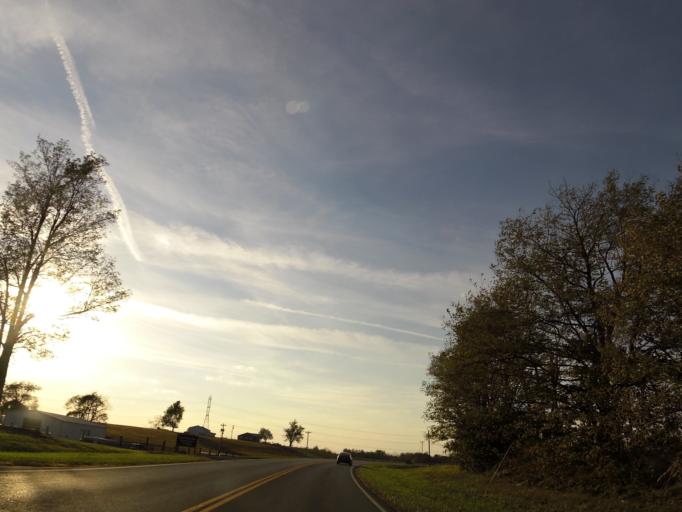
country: US
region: Kentucky
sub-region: Garrard County
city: Lancaster
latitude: 37.6679
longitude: -84.6293
